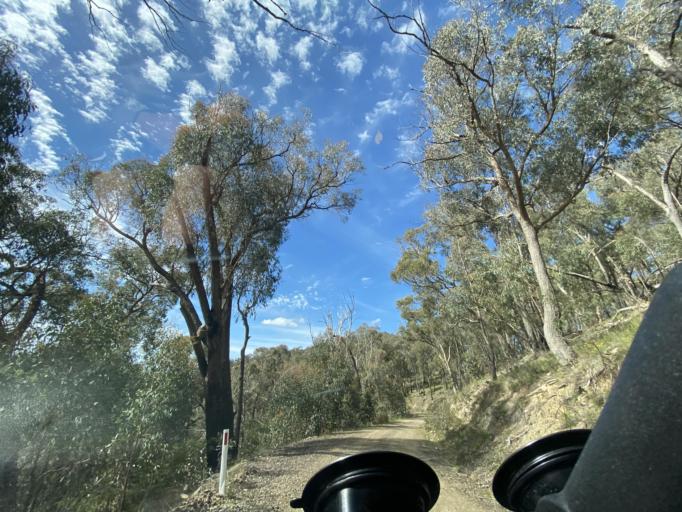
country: AU
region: Victoria
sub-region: Mansfield
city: Mansfield
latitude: -36.8074
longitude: 146.1070
